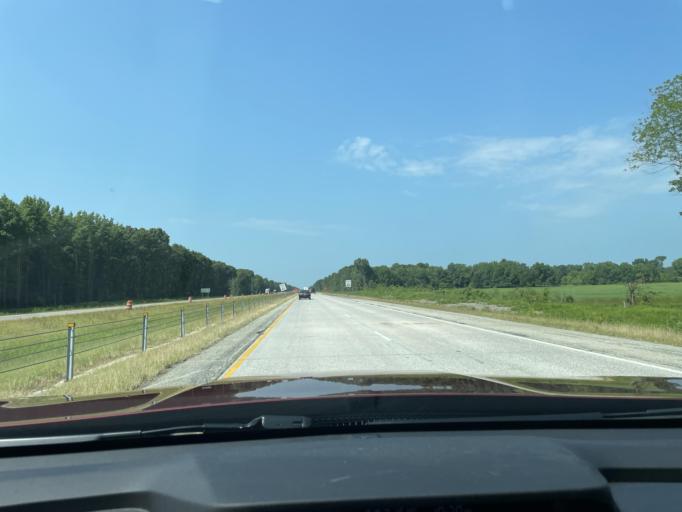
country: US
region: Arkansas
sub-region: White County
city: Searcy
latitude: 35.1870
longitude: -91.7517
